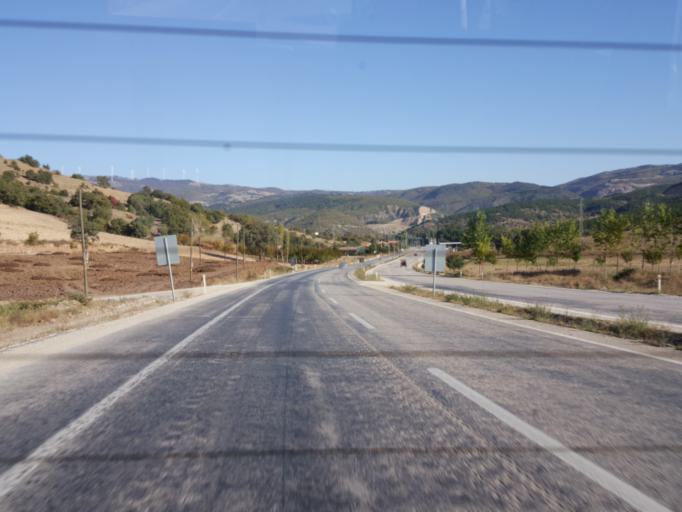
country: TR
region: Amasya
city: Ezinepazari
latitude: 40.5589
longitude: 36.1381
